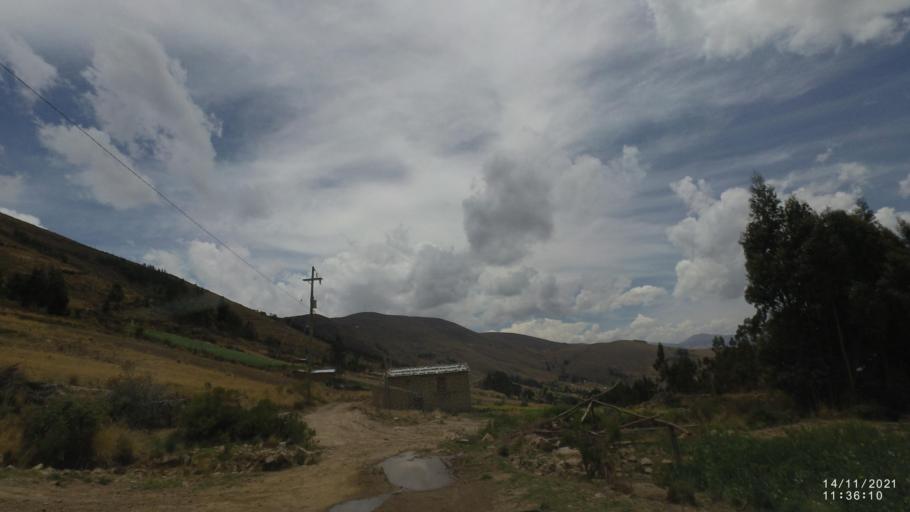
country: BO
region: Cochabamba
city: Colomi
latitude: -17.3462
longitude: -65.9990
